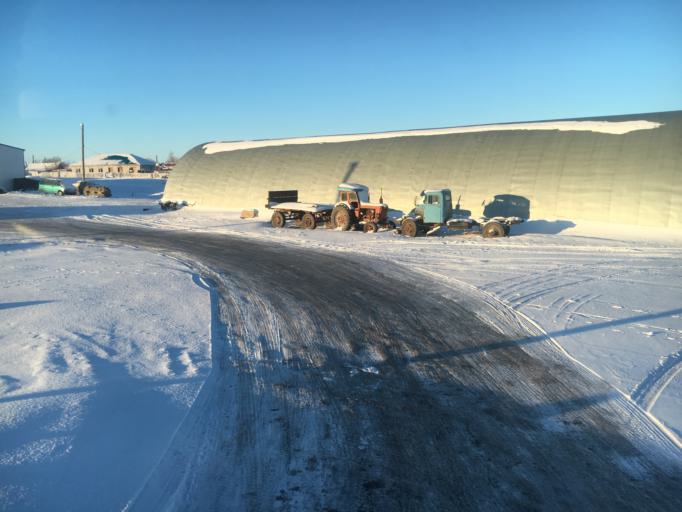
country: KZ
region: Aqtoebe
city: Khromtau
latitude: 50.2506
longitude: 58.5001
